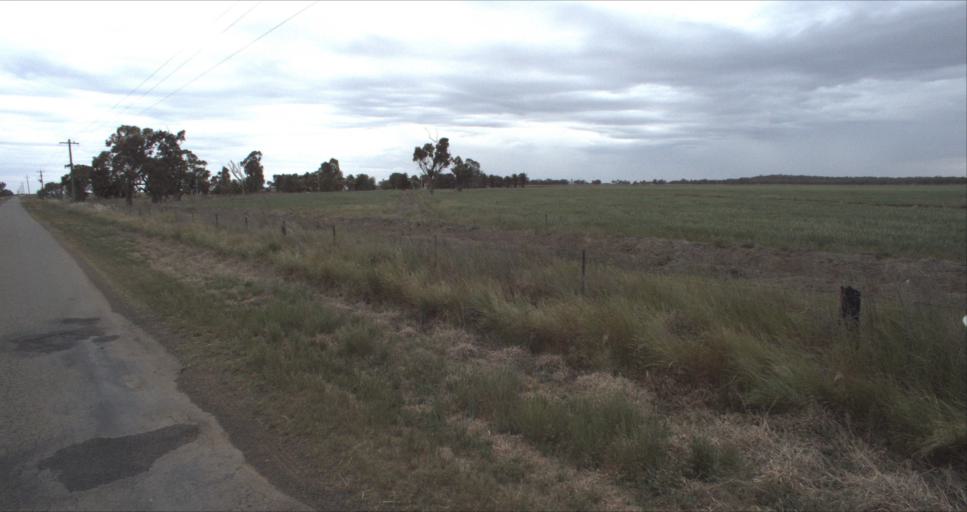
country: AU
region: New South Wales
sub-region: Leeton
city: Leeton
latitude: -34.4187
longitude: 146.3389
